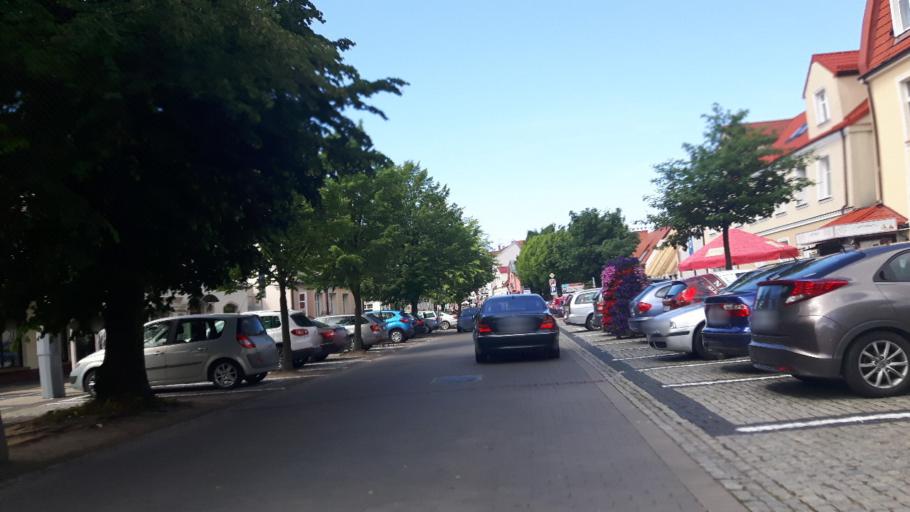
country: PL
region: Pomeranian Voivodeship
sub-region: Powiat slupski
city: Ustka
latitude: 54.5822
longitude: 16.8588
